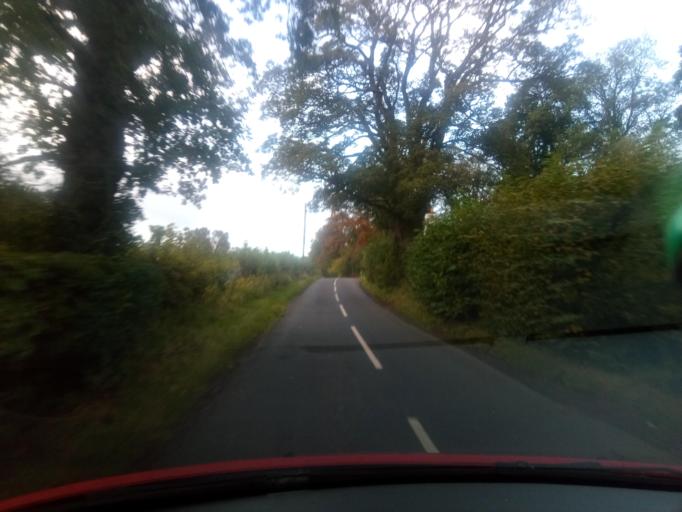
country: GB
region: Scotland
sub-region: The Scottish Borders
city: Jedburgh
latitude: 55.4120
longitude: -2.6467
